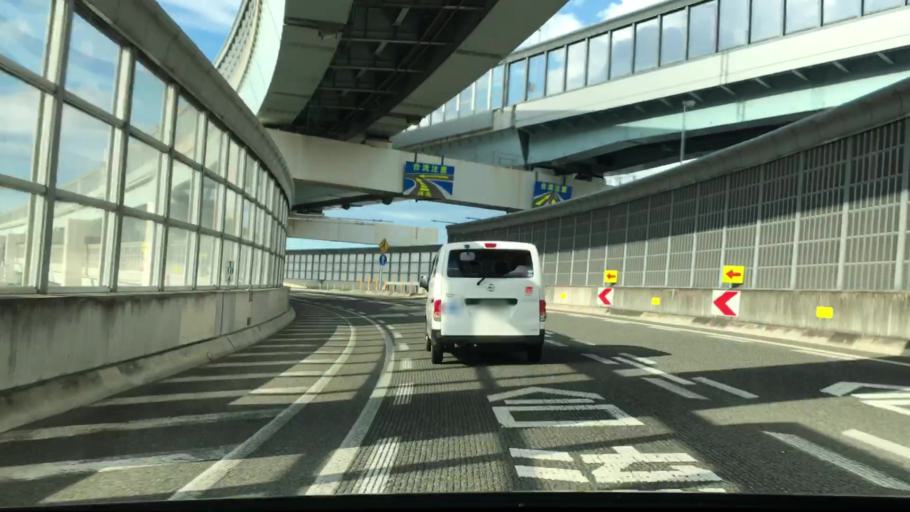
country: JP
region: Fukuoka
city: Fukuoka-shi
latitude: 33.5696
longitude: 130.3169
